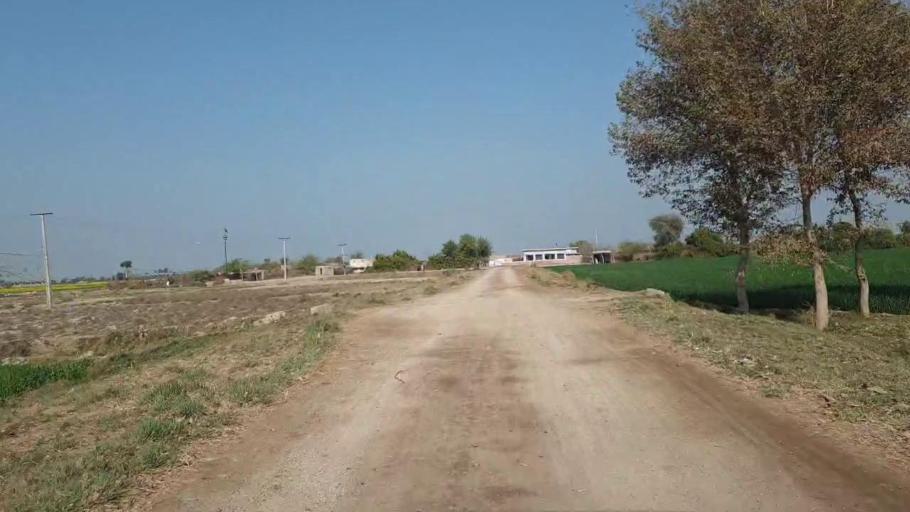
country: PK
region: Sindh
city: Hala
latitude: 25.9464
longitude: 68.4337
